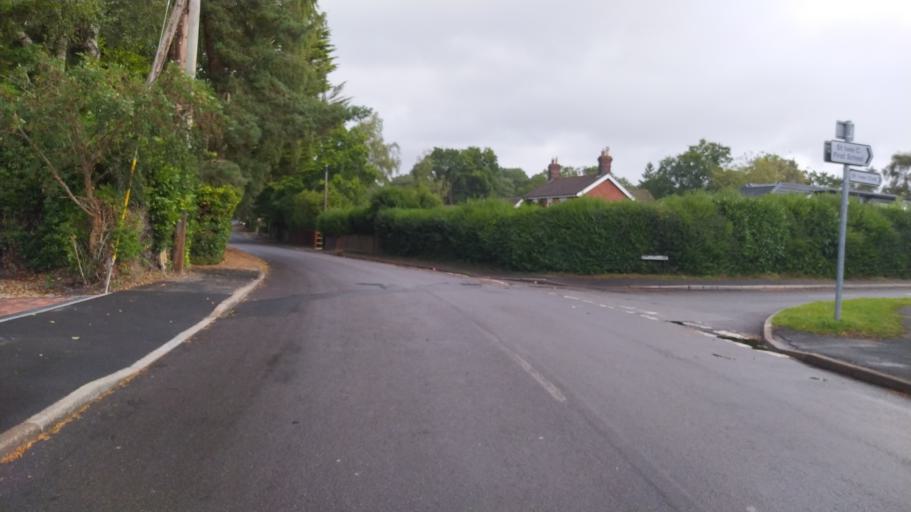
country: GB
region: England
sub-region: Dorset
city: St Leonards
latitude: 50.8333
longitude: -1.8377
